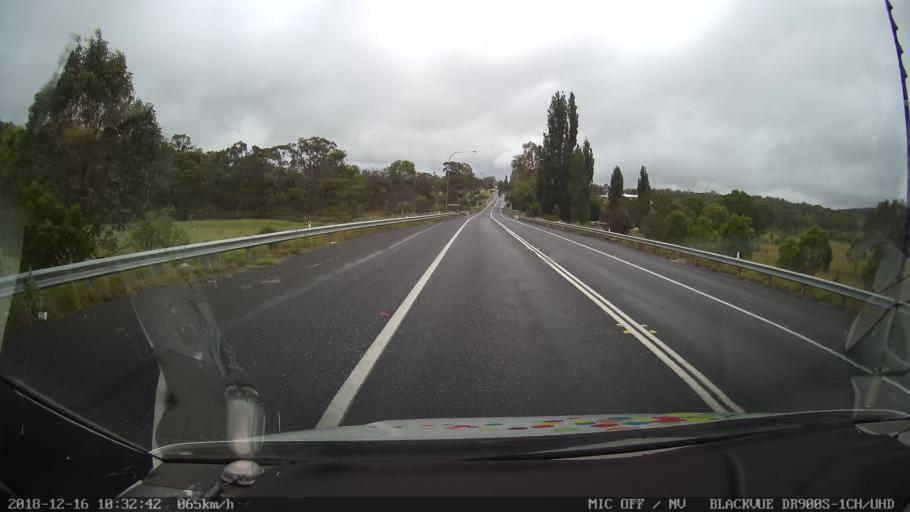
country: AU
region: New South Wales
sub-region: Tenterfield Municipality
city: Carrolls Creek
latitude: -29.0699
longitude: 152.0130
